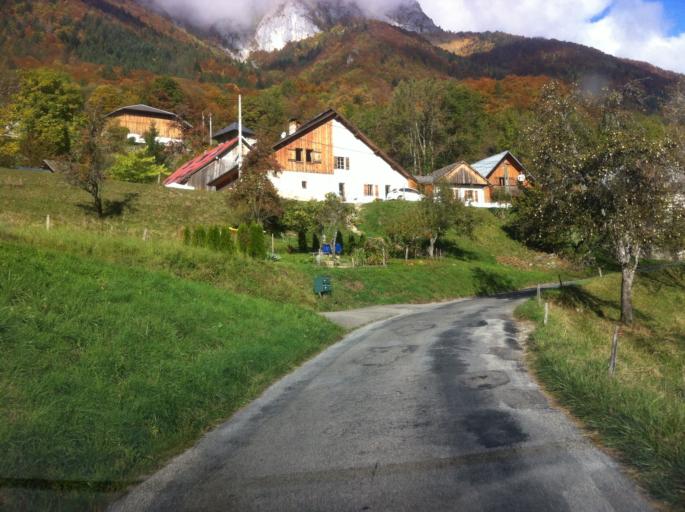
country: FR
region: Rhone-Alpes
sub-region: Departement de la Haute-Savoie
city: Faverges
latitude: 45.7753
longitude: 6.3089
